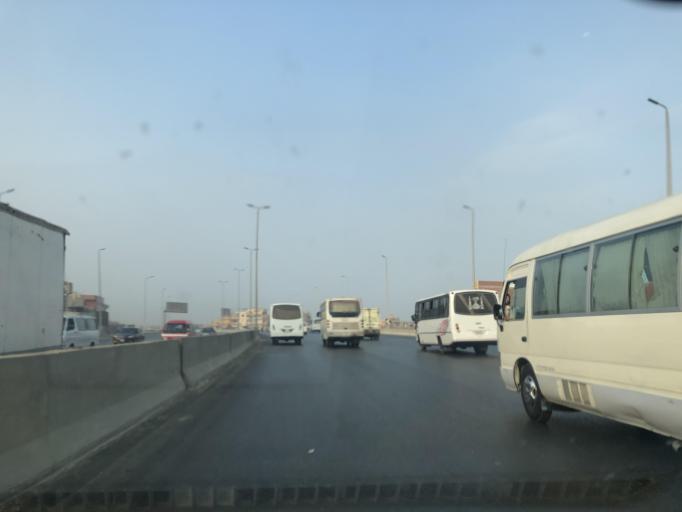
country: EG
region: Muhafazat al Qalyubiyah
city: Qalyub
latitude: 30.1418
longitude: 31.2078
